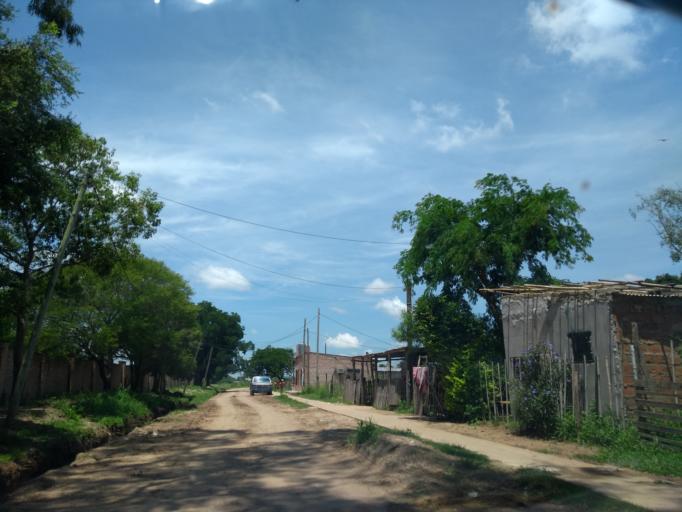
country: AR
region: Chaco
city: Resistencia
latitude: -27.4524
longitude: -58.9595
